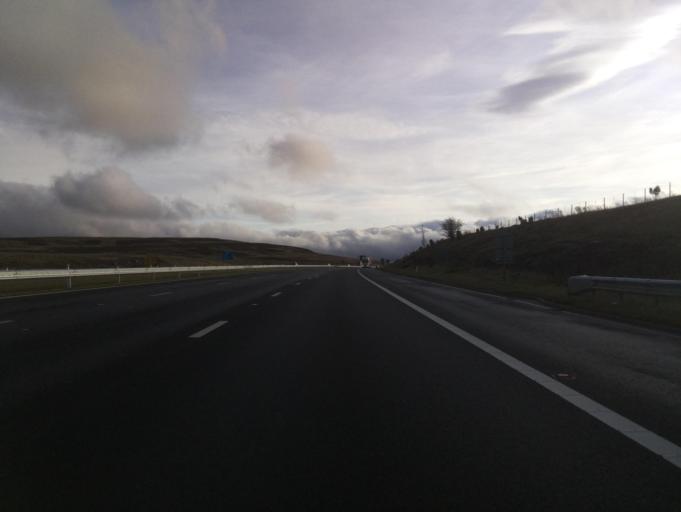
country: GB
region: England
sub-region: Cumbria
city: Appleby-in-Westmorland
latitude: 54.5021
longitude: -2.6454
